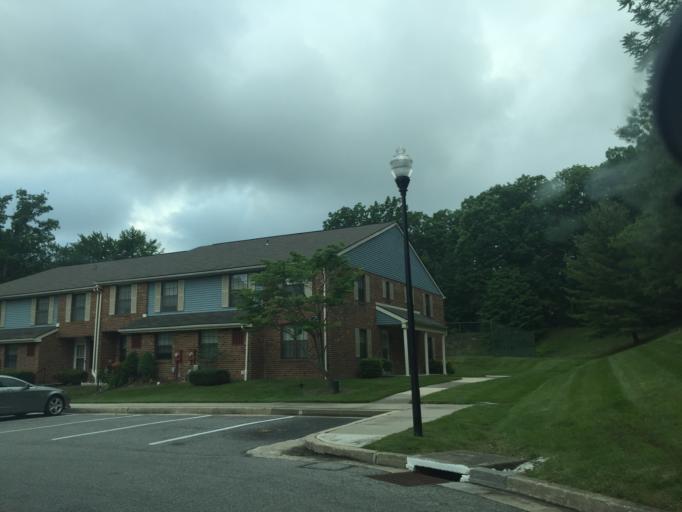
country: US
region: Maryland
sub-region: Baltimore County
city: Carney
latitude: 39.4005
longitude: -76.4927
